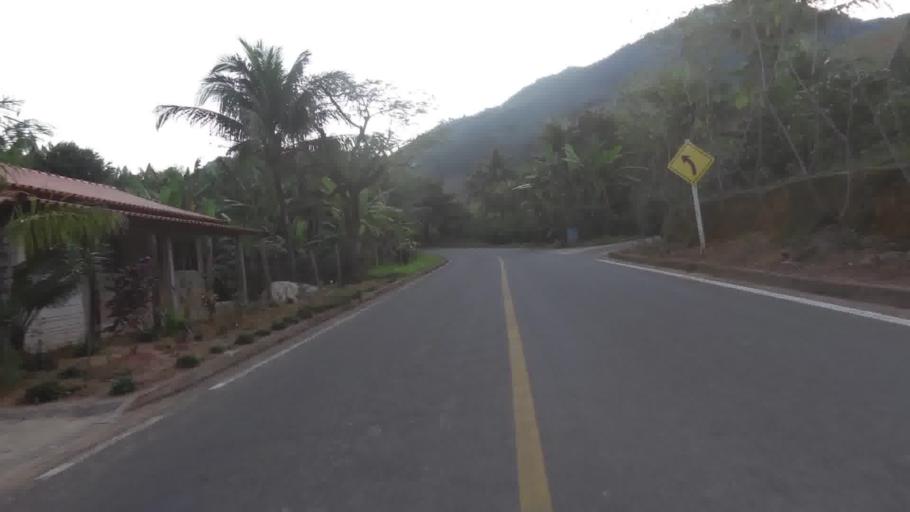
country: BR
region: Espirito Santo
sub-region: Alfredo Chaves
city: Alfredo Chaves
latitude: -20.6013
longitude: -40.7197
